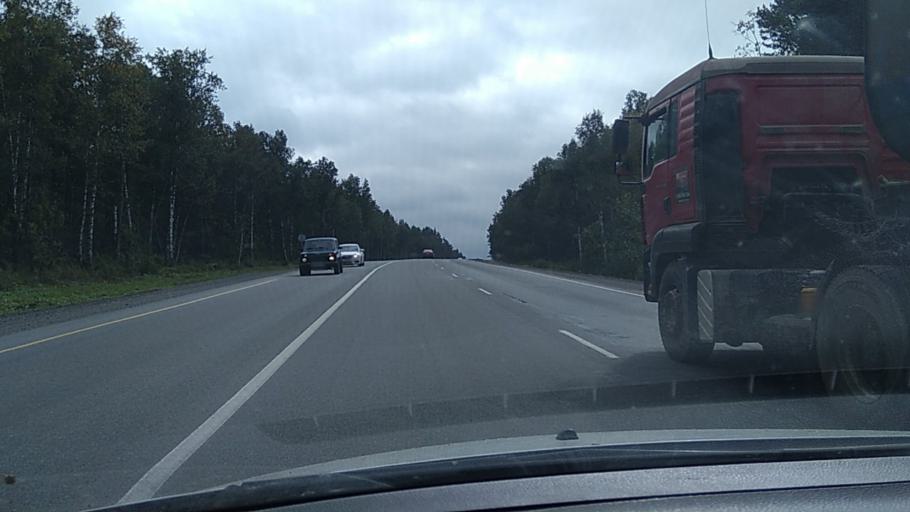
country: RU
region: Chelyabinsk
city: Zlatoust
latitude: 55.0415
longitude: 59.7247
